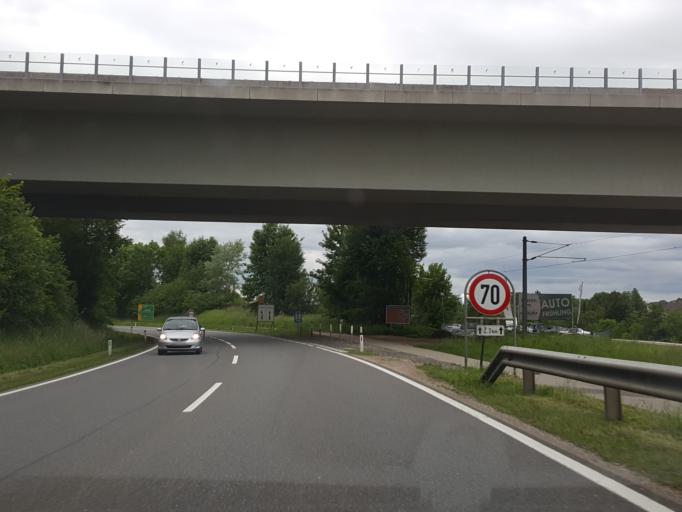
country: AT
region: Upper Austria
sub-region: Politischer Bezirk Vocklabruck
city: Seewalchen
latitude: 47.9517
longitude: 13.6051
